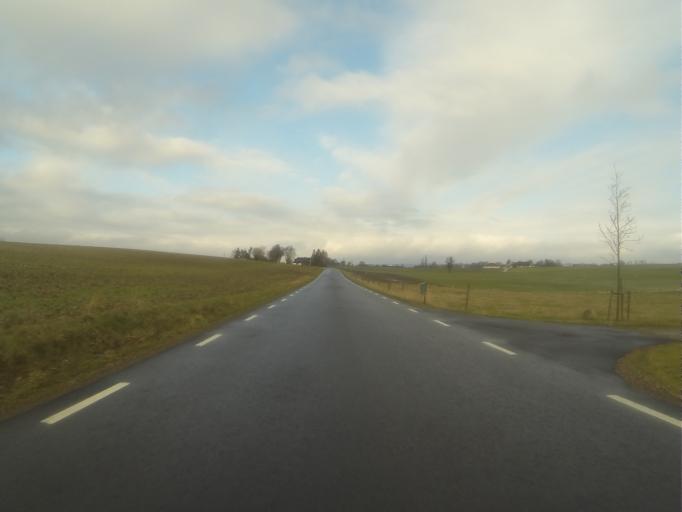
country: SE
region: Skane
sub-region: Svedala Kommun
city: Klagerup
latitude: 55.6172
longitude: 13.3086
